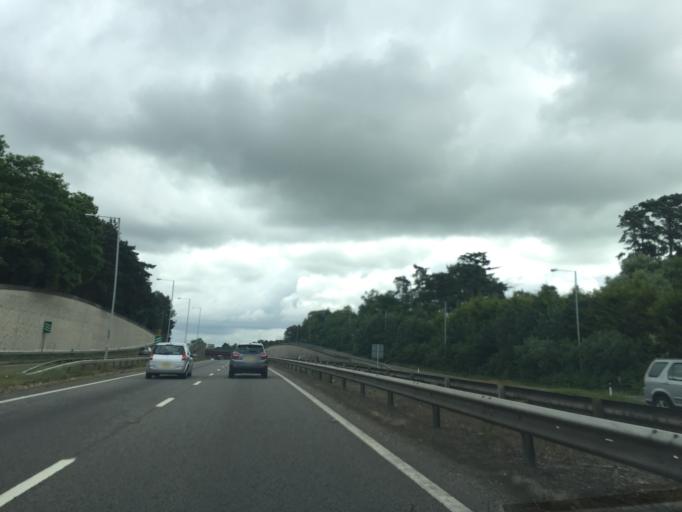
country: GB
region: England
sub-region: Hampshire
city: Ringwood
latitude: 50.8368
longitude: -1.8186
